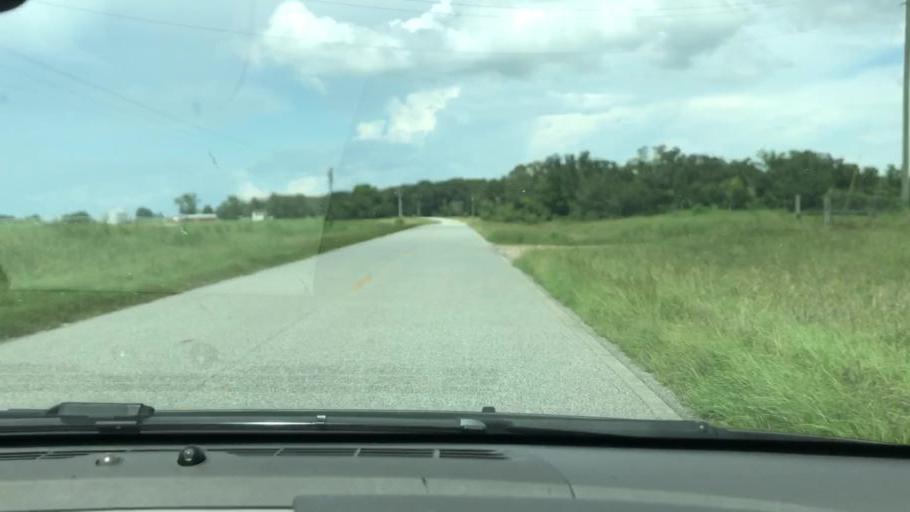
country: US
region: Georgia
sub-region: Seminole County
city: Donalsonville
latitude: 31.0773
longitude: -84.9977
